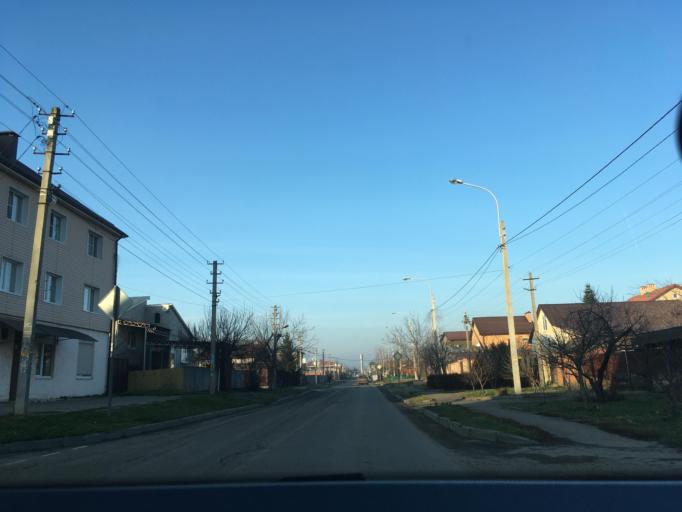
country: RU
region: Krasnodarskiy
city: Krasnodar
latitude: 45.1207
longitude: 39.0143
